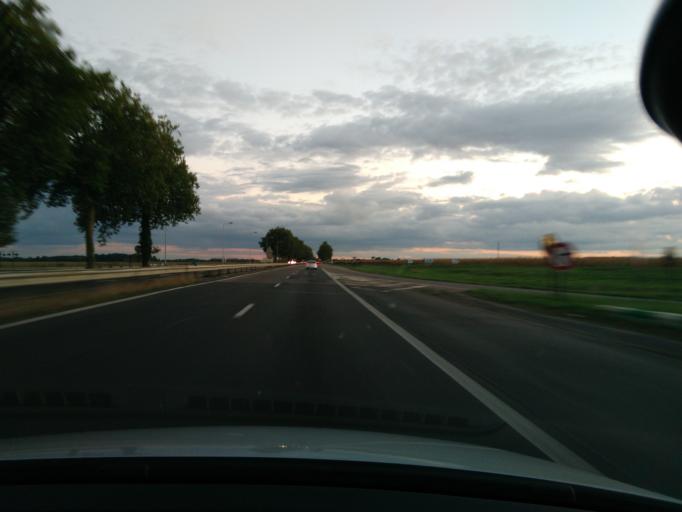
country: FR
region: Ile-de-France
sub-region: Departement de Seine-et-Marne
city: Nanteuil-les-Meaux
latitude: 48.9272
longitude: 2.8804
